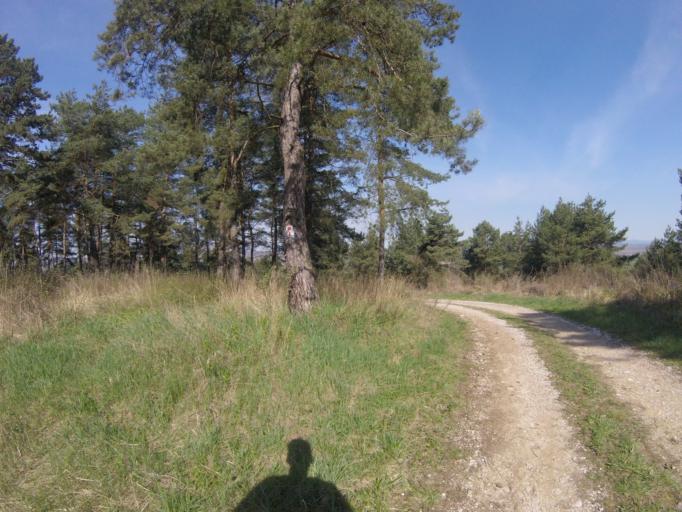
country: HU
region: Borsod-Abauj-Zemplen
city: Szendro
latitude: 48.4086
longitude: 20.7361
